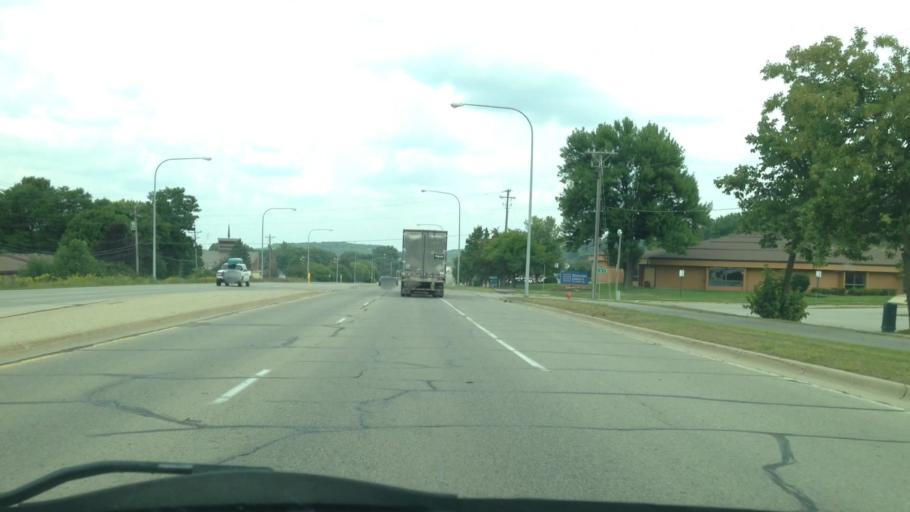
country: US
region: Minnesota
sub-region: Olmsted County
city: Rochester
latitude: 44.0494
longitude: -92.4556
